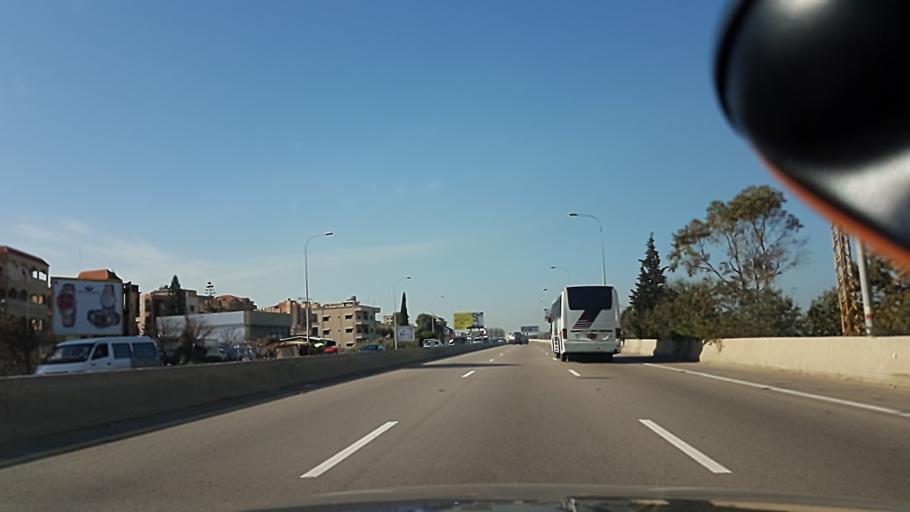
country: LB
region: Liban-Sud
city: Sidon
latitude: 33.6070
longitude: 35.4002
